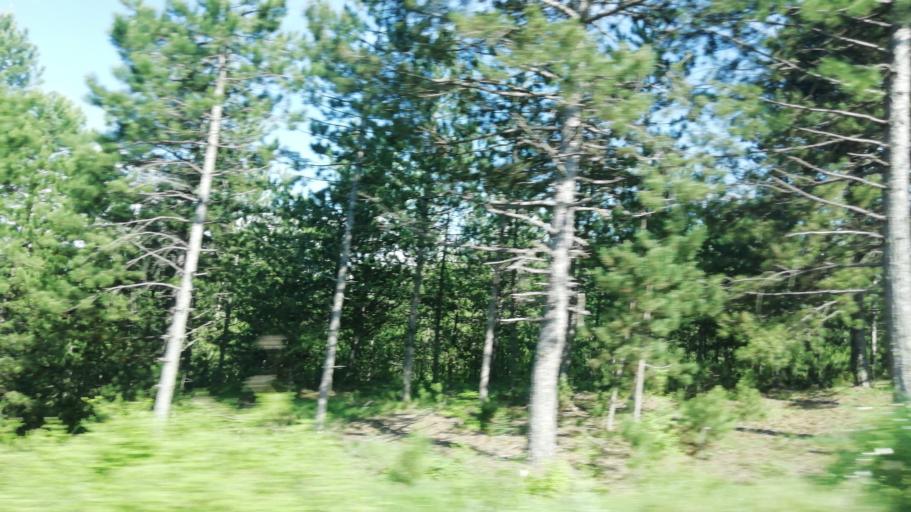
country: TR
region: Karabuk
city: Karabuk
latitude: 41.1233
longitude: 32.6053
